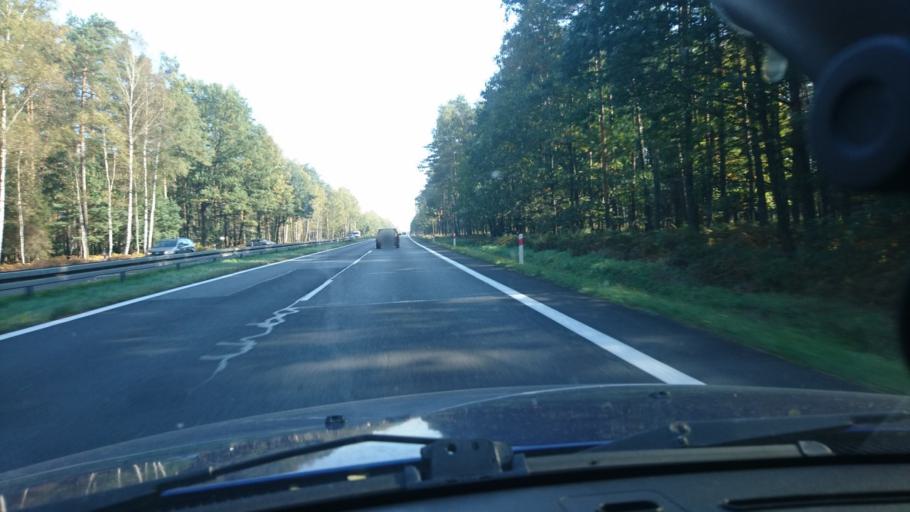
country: PL
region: Silesian Voivodeship
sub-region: Powiat pszczynski
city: Kobior
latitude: 50.0640
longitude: 18.9719
